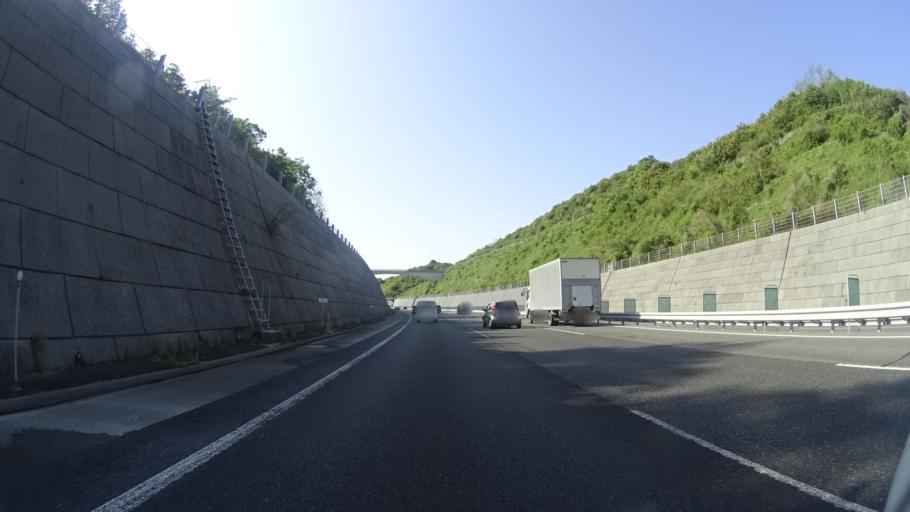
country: JP
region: Hyogo
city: Akashi
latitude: 34.5969
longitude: 135.0068
